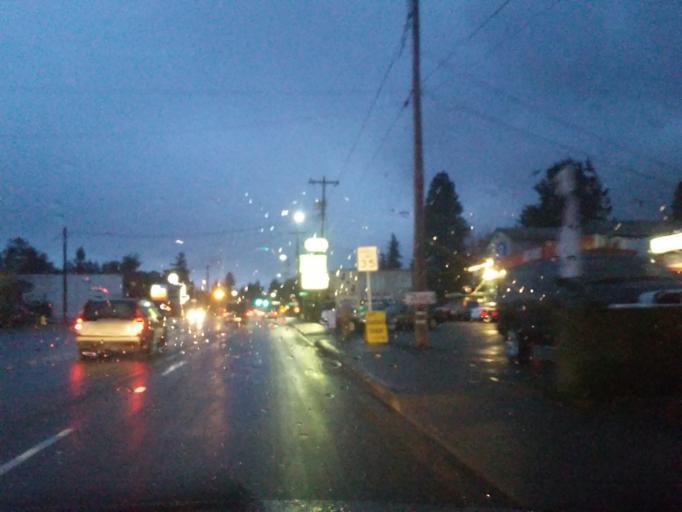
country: US
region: Washington
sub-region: King County
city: Shoreline
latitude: 47.7350
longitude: -122.3127
